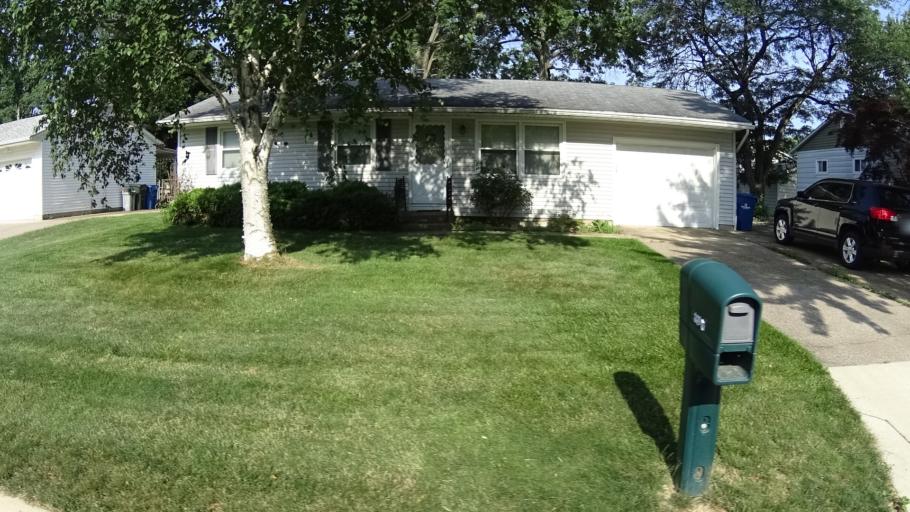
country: US
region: Ohio
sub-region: Lorain County
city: Vermilion
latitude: 41.4122
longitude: -82.3556
